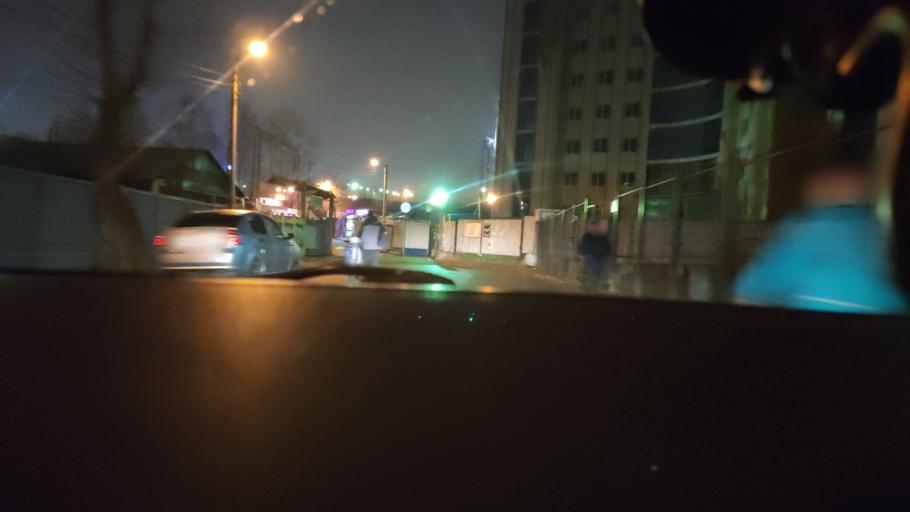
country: RU
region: Perm
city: Perm
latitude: 58.0062
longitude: 56.1841
